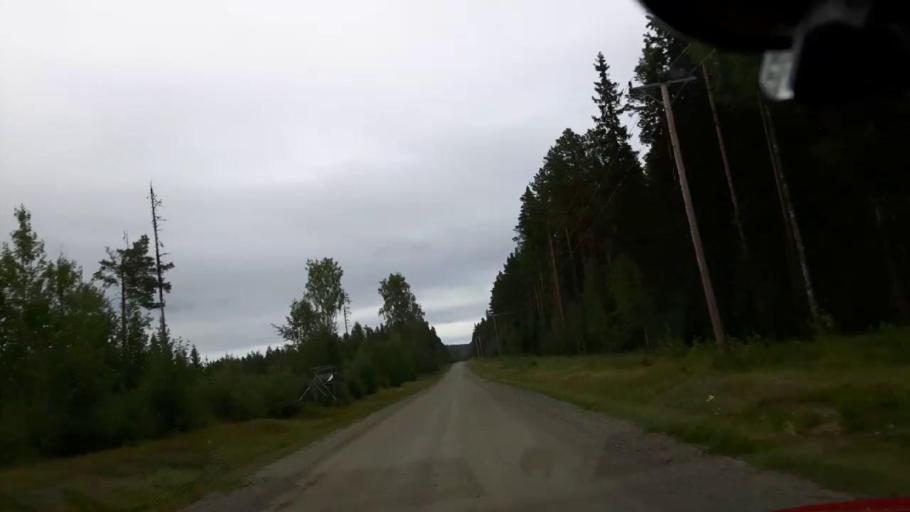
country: SE
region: Vaesternorrland
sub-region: Ange Kommun
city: Fransta
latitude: 62.8587
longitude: 15.9961
